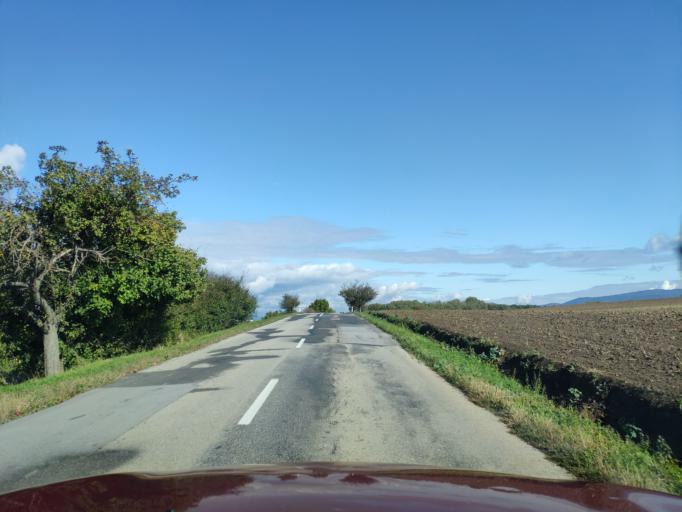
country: SK
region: Presovsky
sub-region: Okres Presov
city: Presov
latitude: 48.8966
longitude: 21.2594
